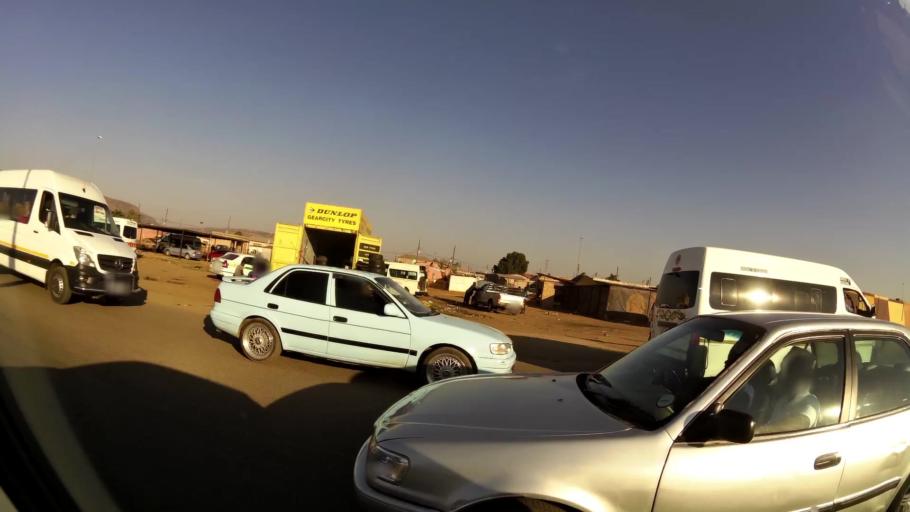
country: ZA
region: Gauteng
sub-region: City of Tshwane Metropolitan Municipality
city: Cullinan
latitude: -25.7100
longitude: 28.4123
